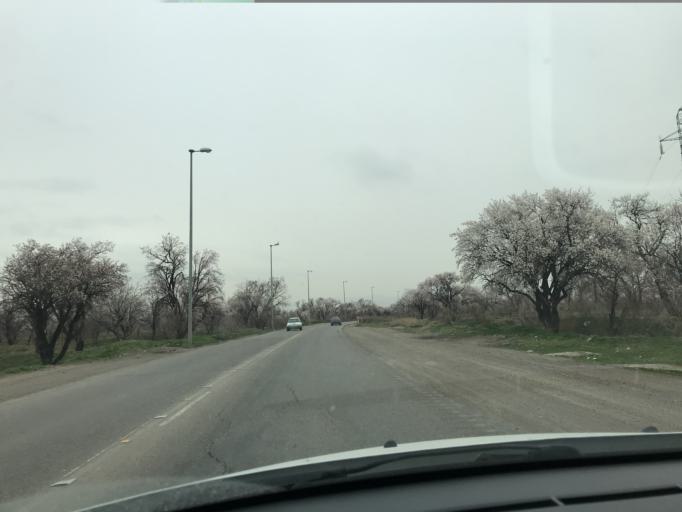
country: IR
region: Qazvin
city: Qazvin
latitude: 36.2771
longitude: 49.9791
